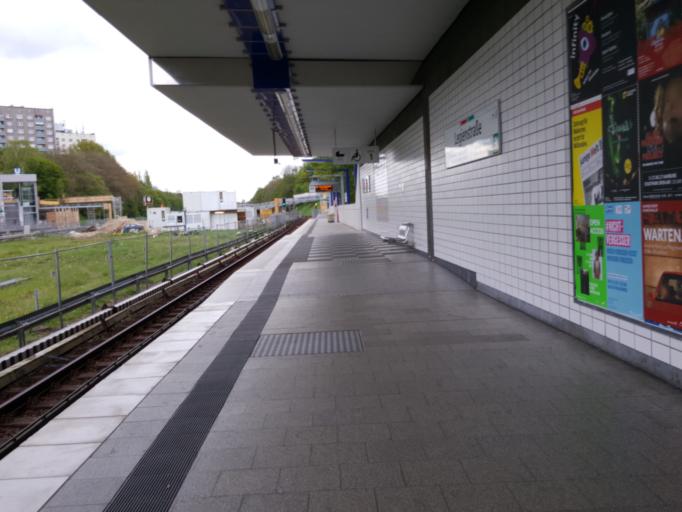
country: DE
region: Hamburg
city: Wandsbek
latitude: 53.5472
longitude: 10.0956
